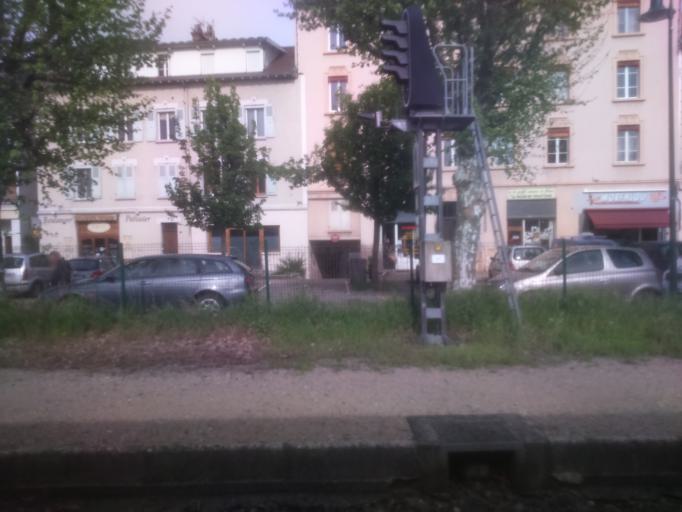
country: FR
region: Rhone-Alpes
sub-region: Departement de l'Isere
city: Champ-sur-Drac
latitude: 45.0848
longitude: 5.7427
